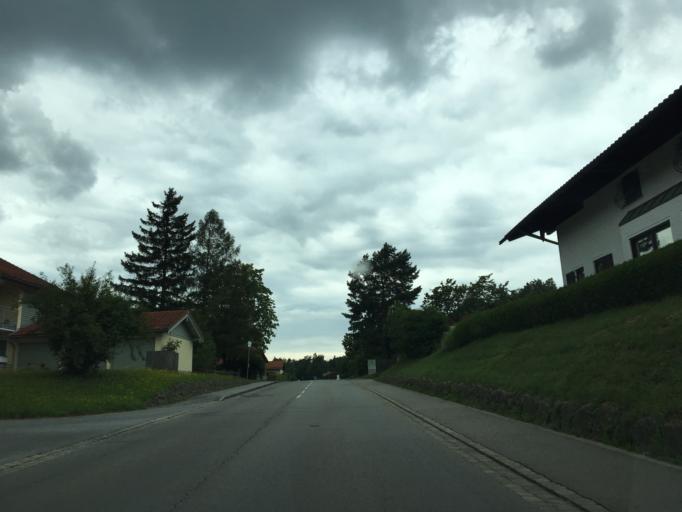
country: DE
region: Bavaria
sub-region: Upper Bavaria
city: Flintsbach
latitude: 47.7140
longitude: 12.1403
